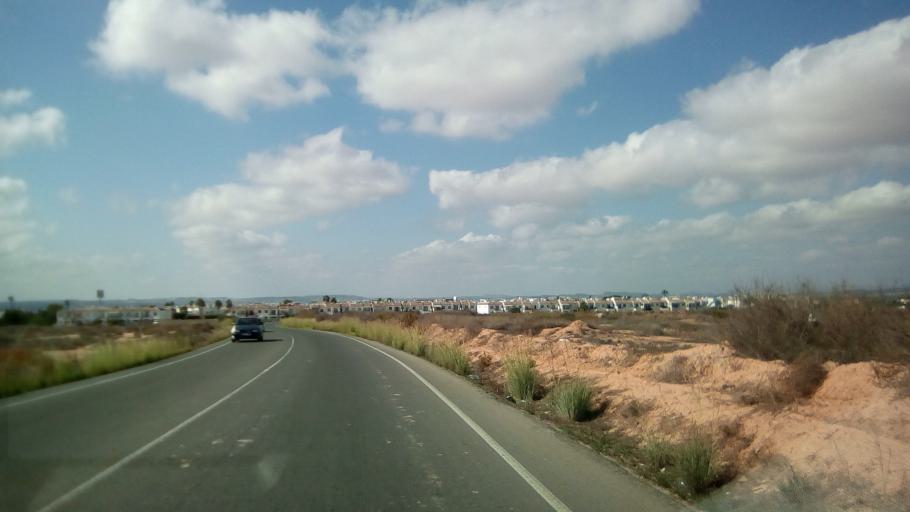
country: ES
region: Valencia
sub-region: Provincia de Alicante
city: Torrevieja
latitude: 37.9997
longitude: -0.6815
